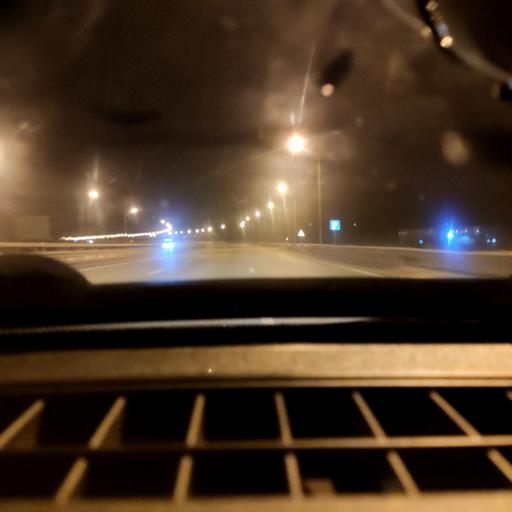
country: RU
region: Bashkortostan
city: Ufa
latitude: 54.6430
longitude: 55.9418
